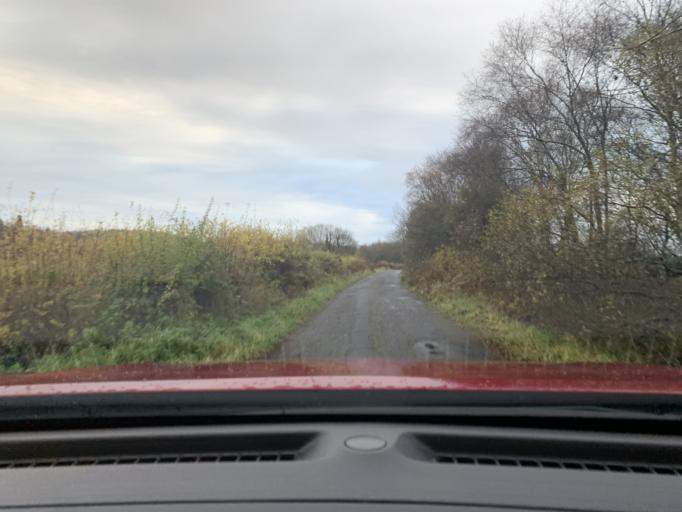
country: IE
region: Connaught
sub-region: Sligo
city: Ballymote
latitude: 54.0147
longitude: -8.5010
